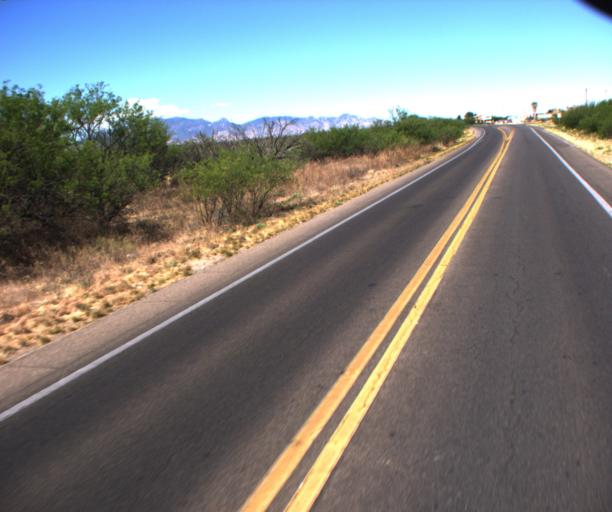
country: US
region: Arizona
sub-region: Cochise County
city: Sierra Vista
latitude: 31.5543
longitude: -110.2043
